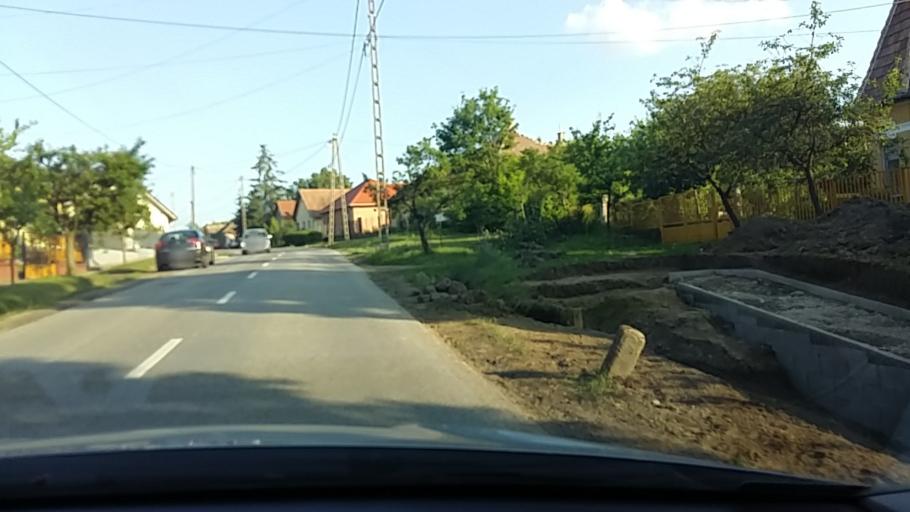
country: HU
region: Pest
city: Szod
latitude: 47.7467
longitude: 19.2098
